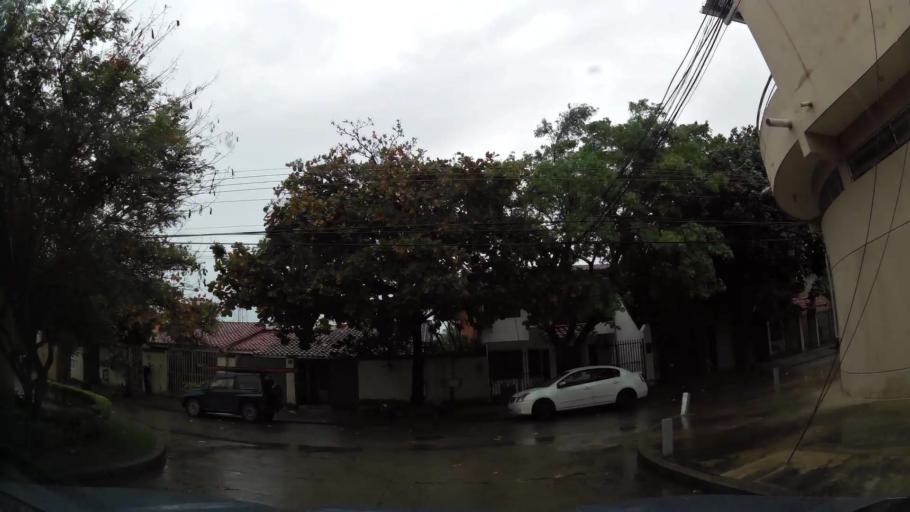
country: BO
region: Santa Cruz
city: Santa Cruz de la Sierra
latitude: -17.7897
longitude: -63.2080
